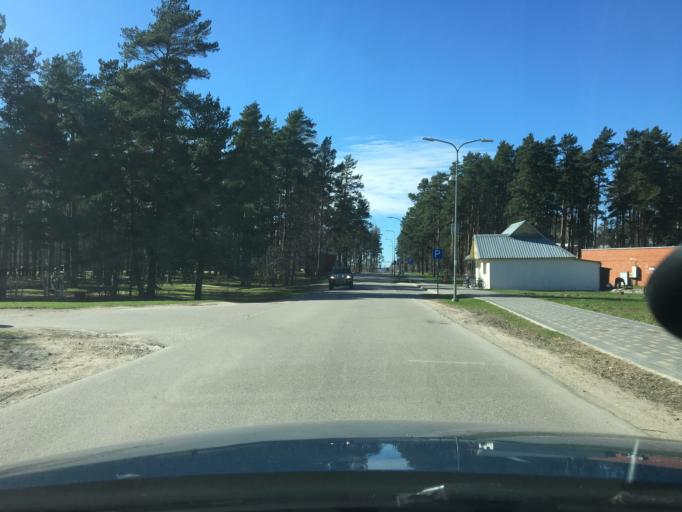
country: LV
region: Salaspils
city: Salaspils
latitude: 56.8701
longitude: 24.3461
